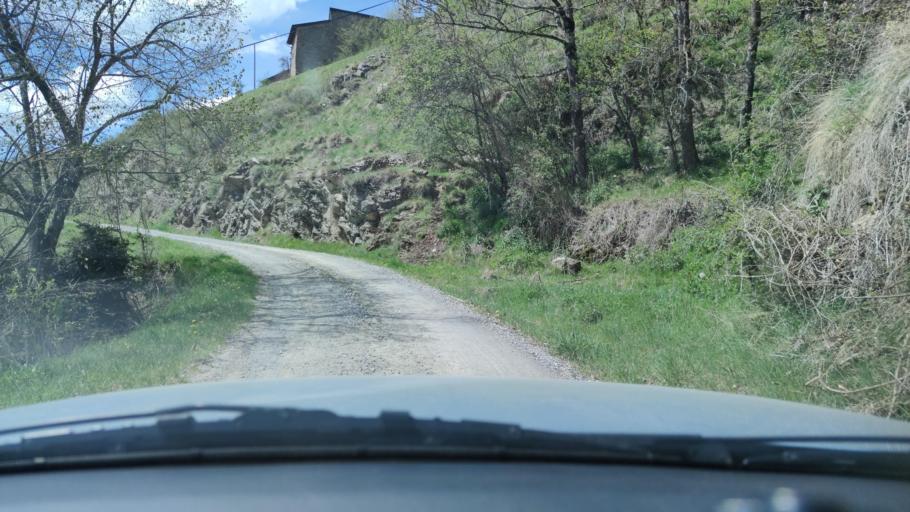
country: ES
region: Catalonia
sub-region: Provincia de Lleida
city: Sort
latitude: 42.2994
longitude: 1.1786
